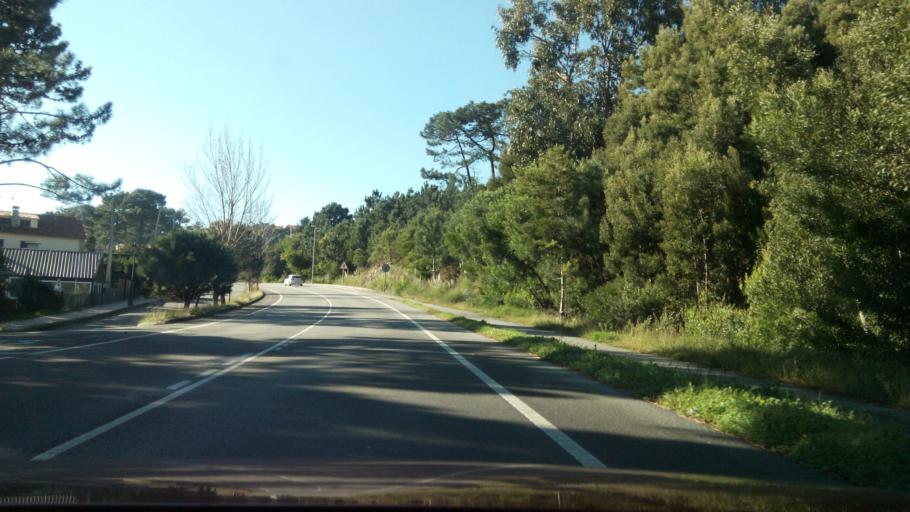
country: ES
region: Galicia
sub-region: Provincia de Pontevedra
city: O Grove
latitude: 42.4599
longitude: -8.9197
